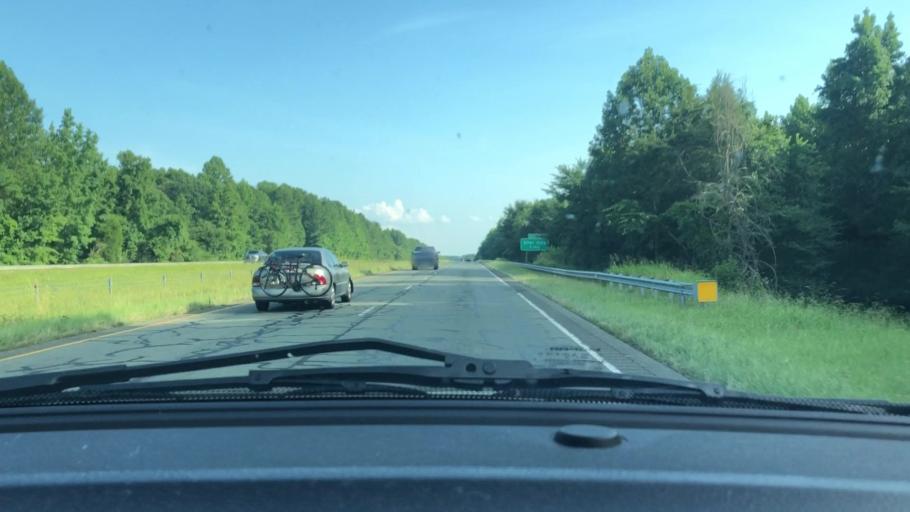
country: US
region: North Carolina
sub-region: Chatham County
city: Siler City
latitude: 35.7145
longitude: -79.4295
